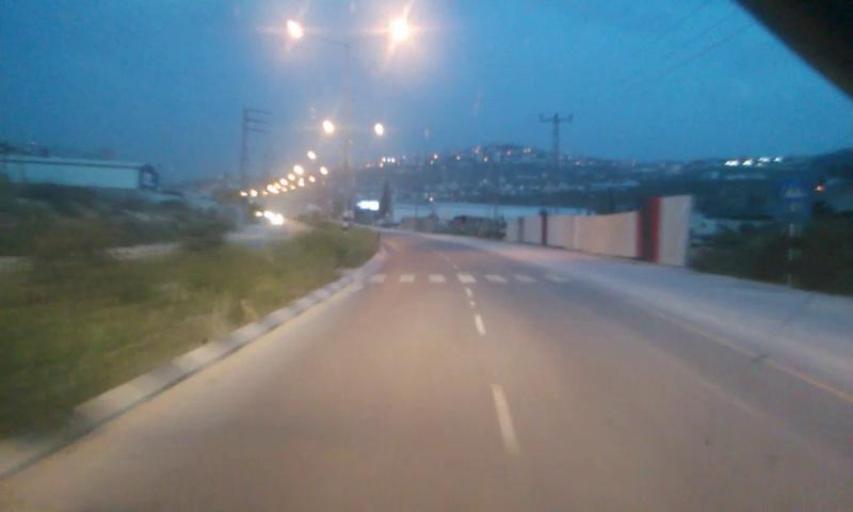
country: PS
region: West Bank
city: Dayr Sharaf
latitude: 32.2440
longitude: 35.1963
